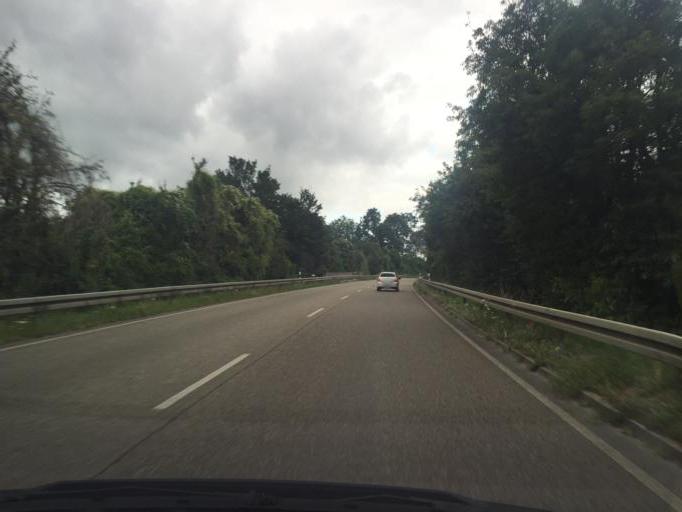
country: DE
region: Baden-Wuerttemberg
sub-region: Karlsruhe Region
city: Gondelsheim
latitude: 49.0996
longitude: 8.6393
